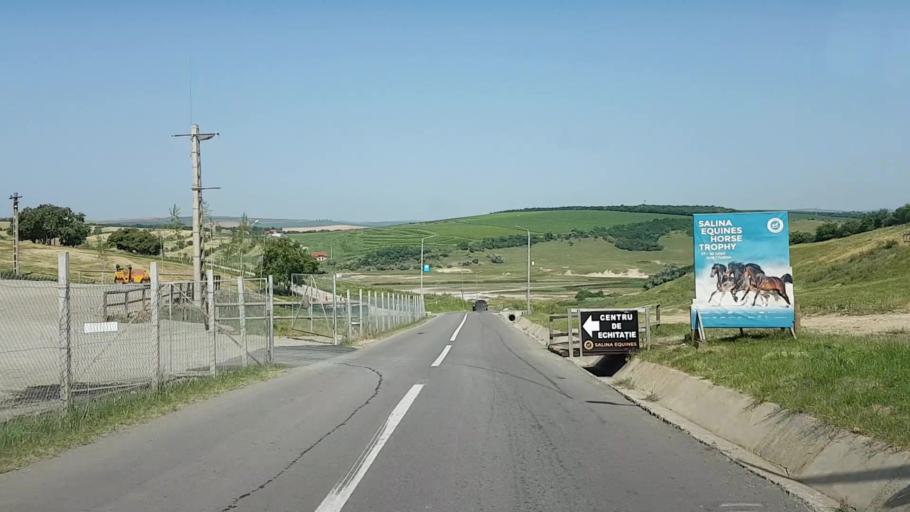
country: RO
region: Cluj
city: Turda
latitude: 46.5859
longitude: 23.7962
